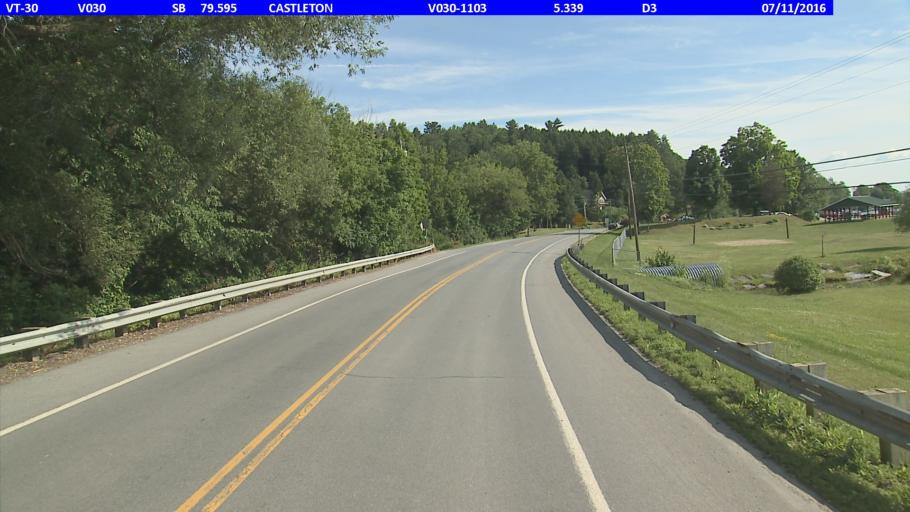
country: US
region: Vermont
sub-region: Rutland County
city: Castleton
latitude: 43.6617
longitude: -73.1902
